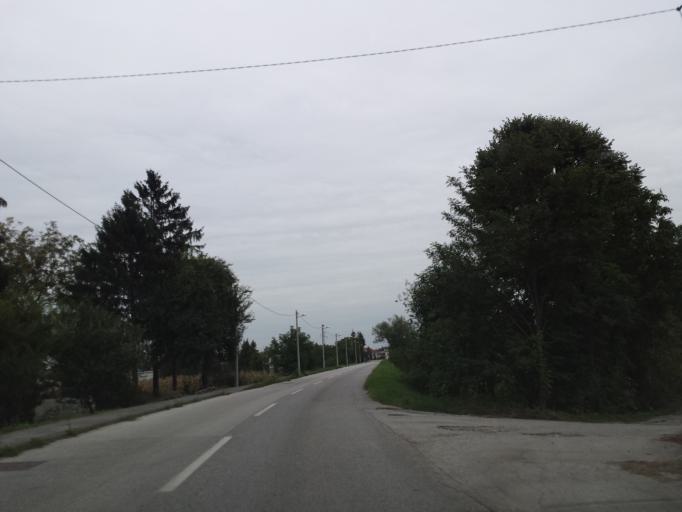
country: HR
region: Grad Zagreb
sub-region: Sesvete
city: Sesvete
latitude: 45.7998
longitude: 16.1147
